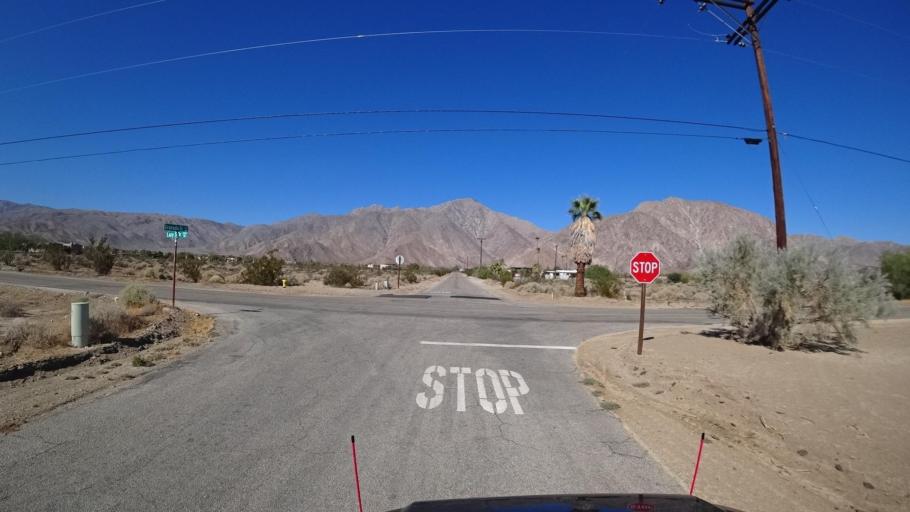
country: US
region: California
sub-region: San Diego County
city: Borrego Springs
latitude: 33.2704
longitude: -116.3853
